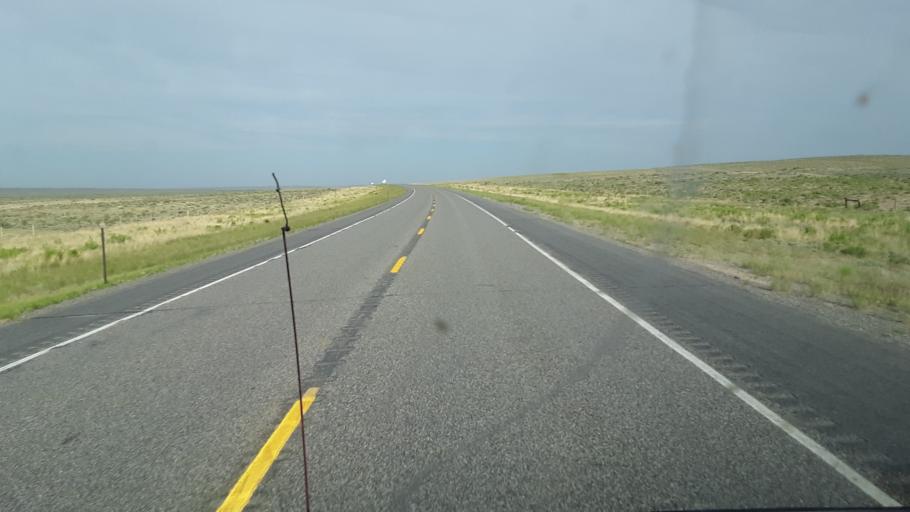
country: US
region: Wyoming
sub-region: Fremont County
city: Riverton
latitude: 43.1640
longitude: -107.7479
